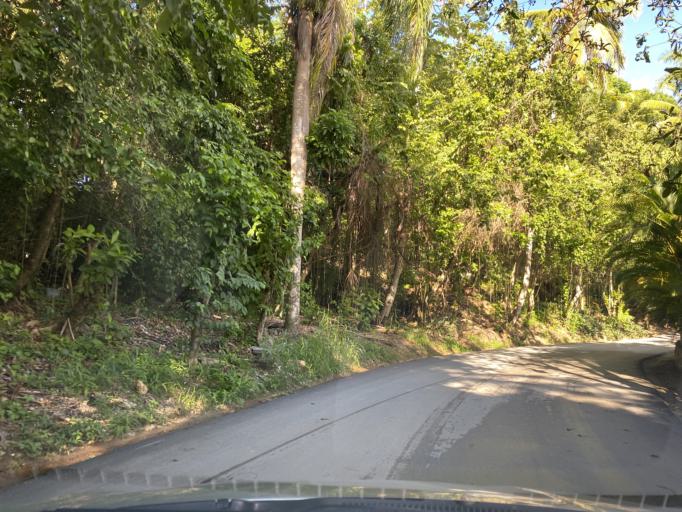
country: DO
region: Samana
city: Las Terrenas
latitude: 19.3185
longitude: -69.5592
